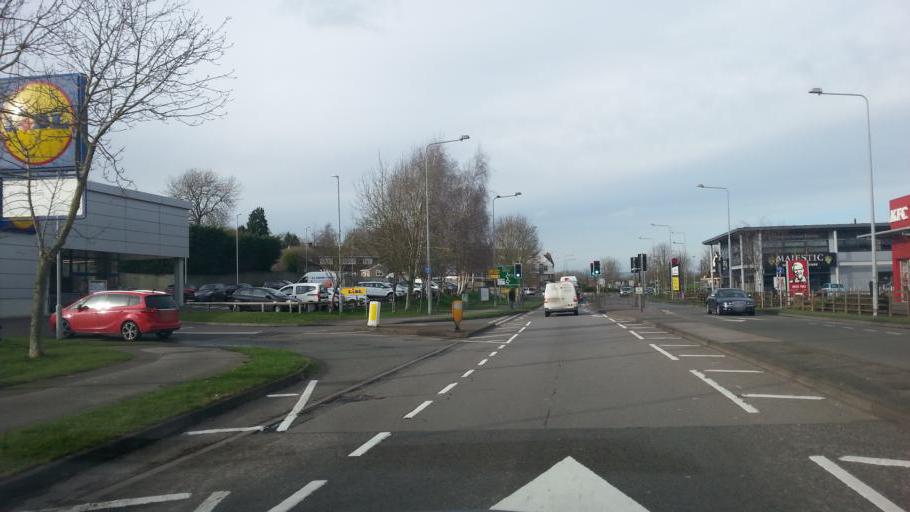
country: GB
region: England
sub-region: Staffordshire
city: Uttoxeter
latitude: 52.8997
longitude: -1.8603
